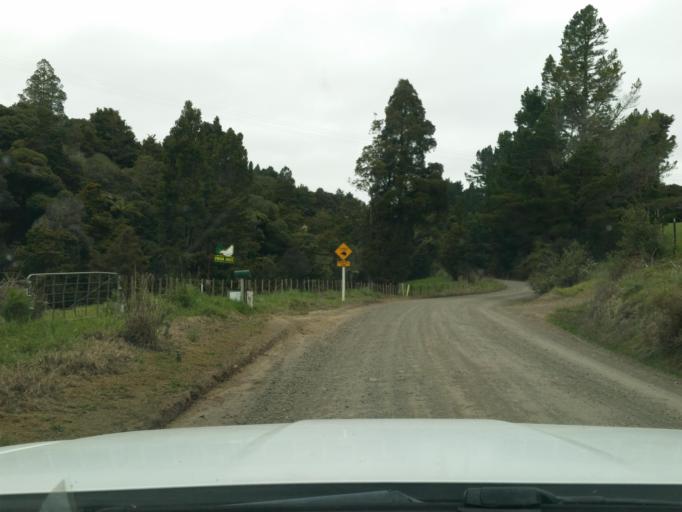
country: NZ
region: Northland
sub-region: Kaipara District
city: Dargaville
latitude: -35.7109
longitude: 173.6240
